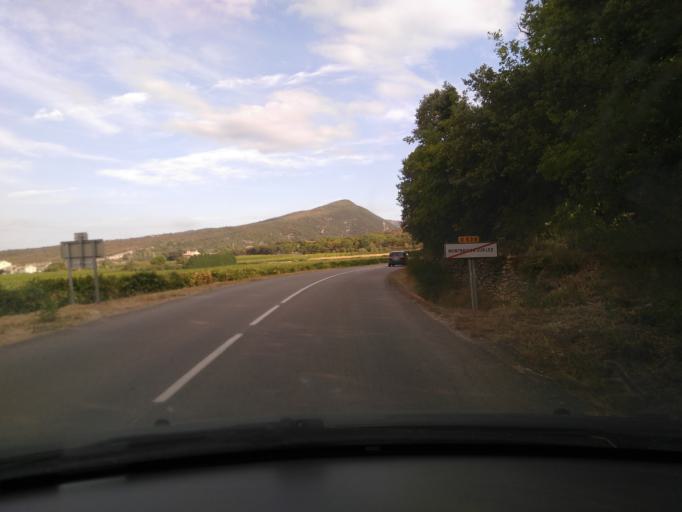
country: FR
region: Rhone-Alpes
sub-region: Departement de la Drome
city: Taulignan
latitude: 44.4385
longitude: 5.0183
